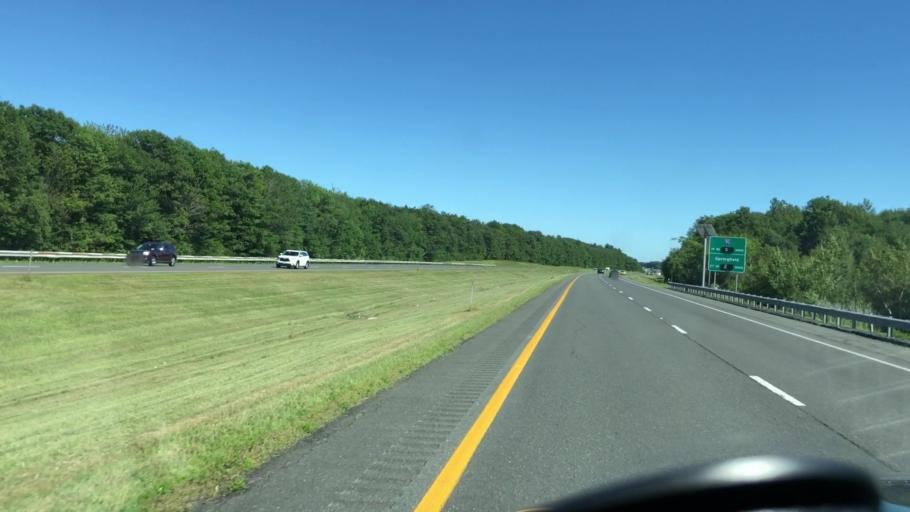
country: US
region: Massachusetts
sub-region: Berkshire County
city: Otis
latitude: 42.2217
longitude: -72.9652
